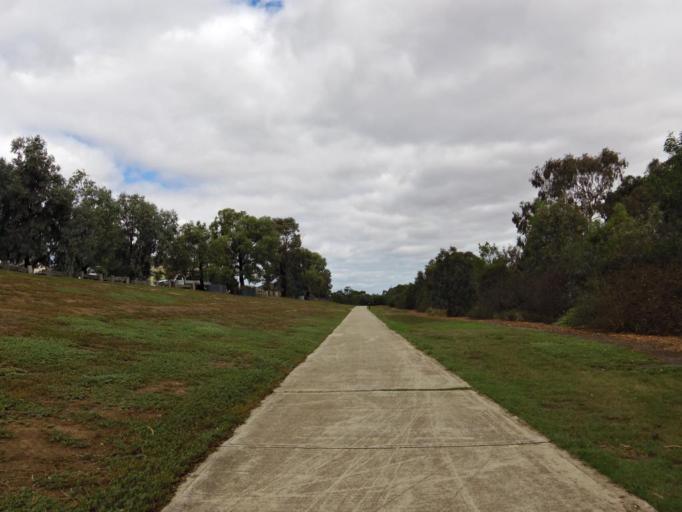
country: AU
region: Victoria
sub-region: Wyndham
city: Werribee
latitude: -37.8886
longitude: 144.6434
